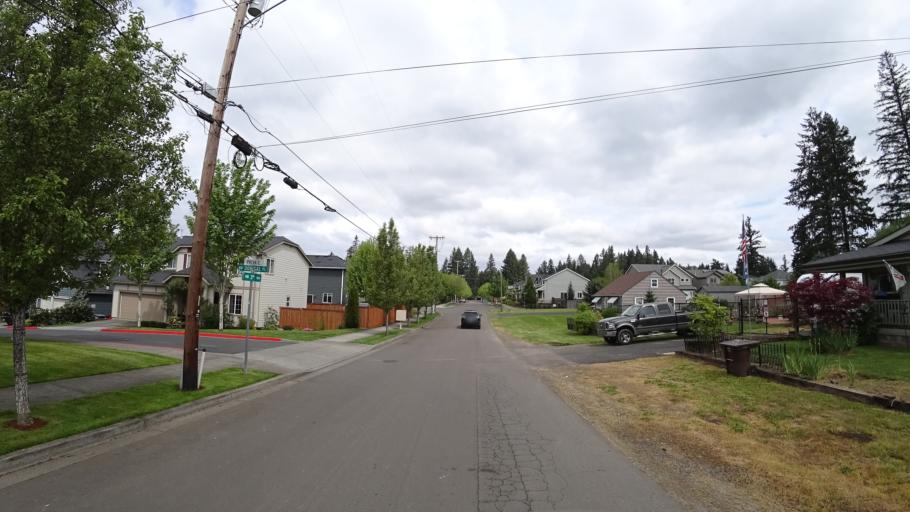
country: US
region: Oregon
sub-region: Washington County
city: Hillsboro
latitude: 45.5460
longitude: -122.9989
